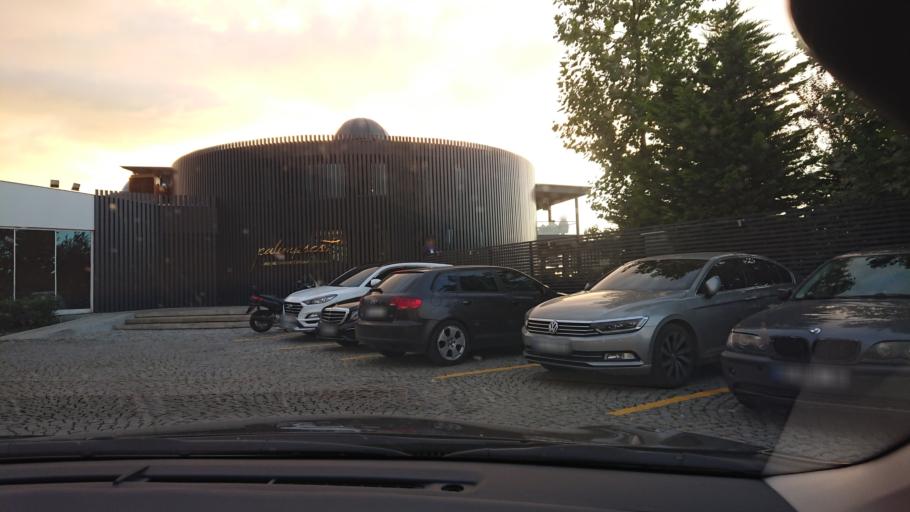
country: TR
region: Rize
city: Rize
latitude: 41.0266
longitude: 40.5273
